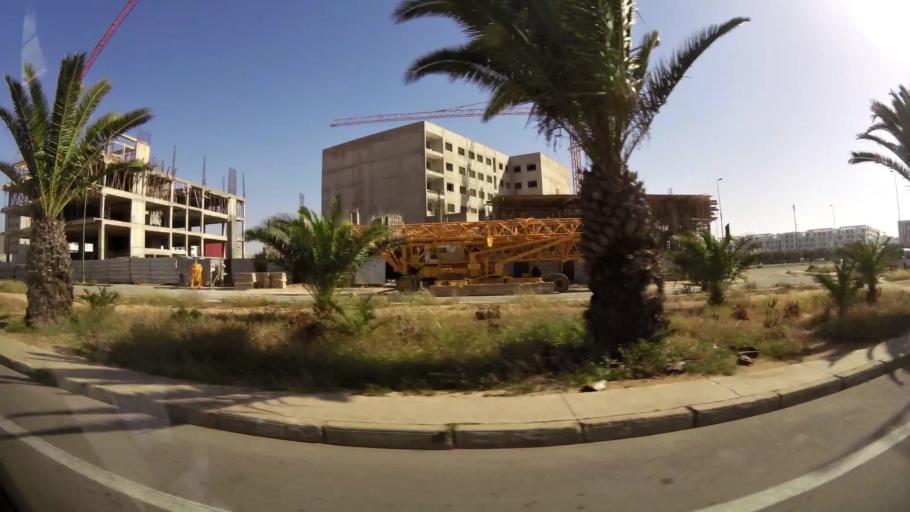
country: MA
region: Souss-Massa-Draa
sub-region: Agadir-Ida-ou-Tnan
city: Agadir
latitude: 30.4029
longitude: -9.5823
